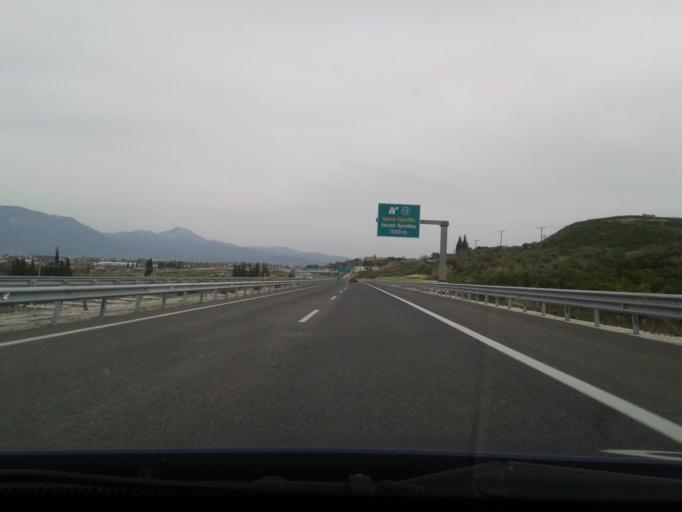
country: GR
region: Peloponnese
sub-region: Nomos Korinthias
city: Arkhaia Korinthos
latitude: 37.9098
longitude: 22.8673
